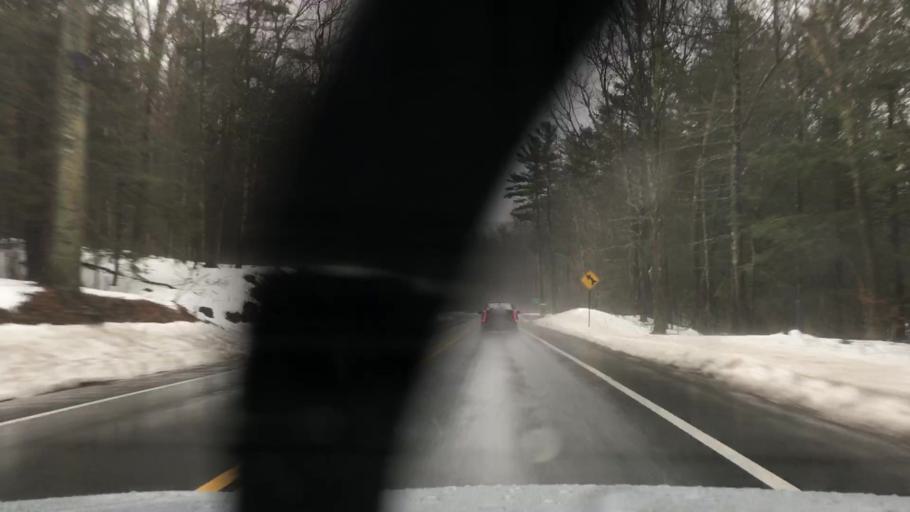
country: US
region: Massachusetts
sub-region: Franklin County
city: Shutesbury
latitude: 42.4778
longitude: -72.3481
